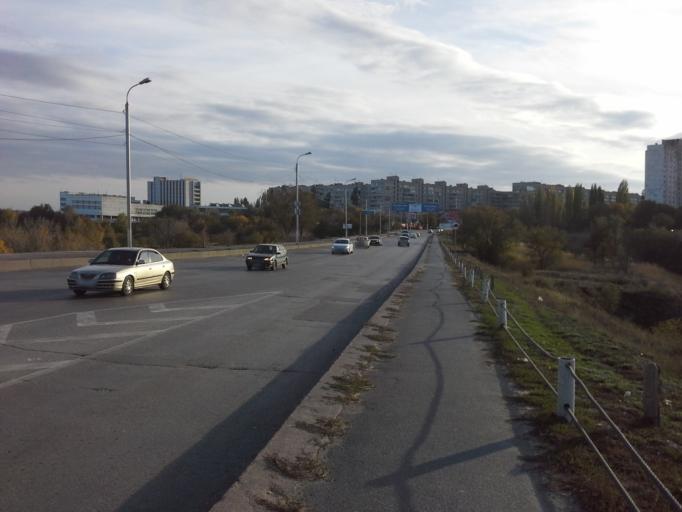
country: RU
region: Volgograd
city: Vodstroy
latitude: 48.8268
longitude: 44.6424
